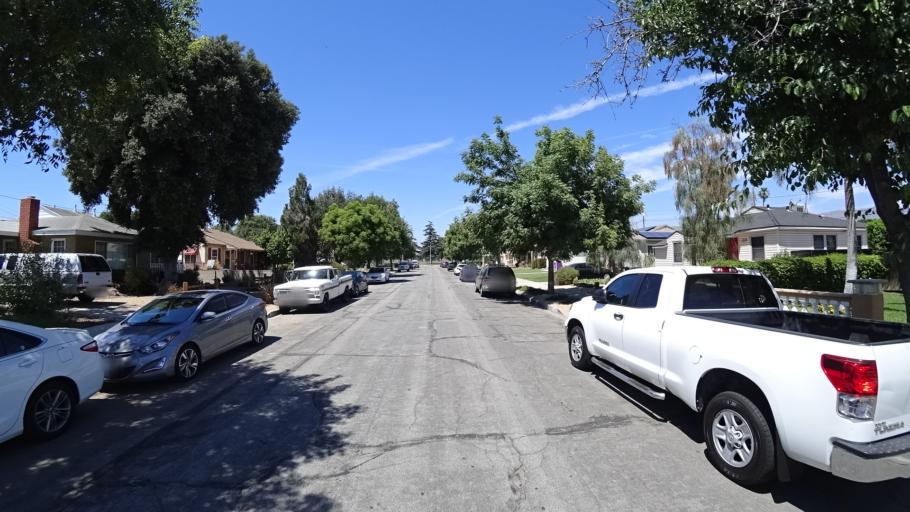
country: US
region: California
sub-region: Los Angeles County
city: North Hollywood
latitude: 34.1873
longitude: -118.3575
